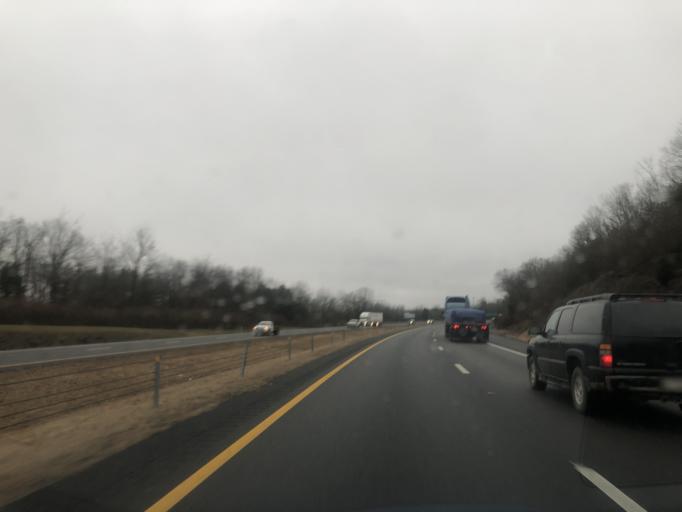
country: US
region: Tennessee
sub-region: Cheatham County
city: Pegram
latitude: 36.0748
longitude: -86.9703
